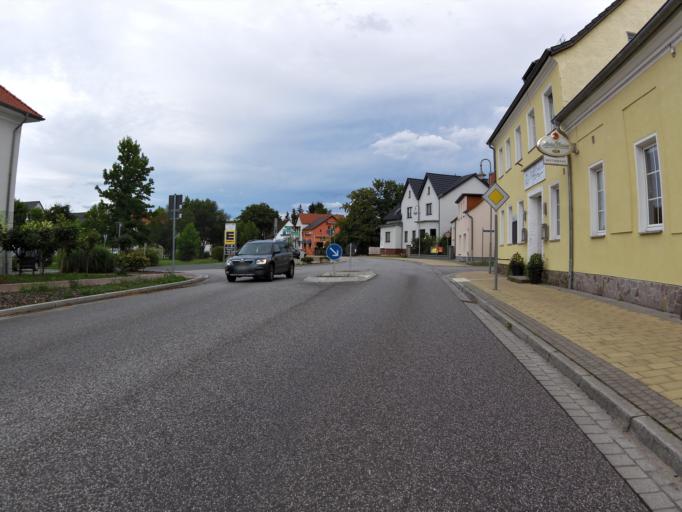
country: DE
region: Brandenburg
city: Wendisch Rietz
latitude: 52.2151
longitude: 14.0050
